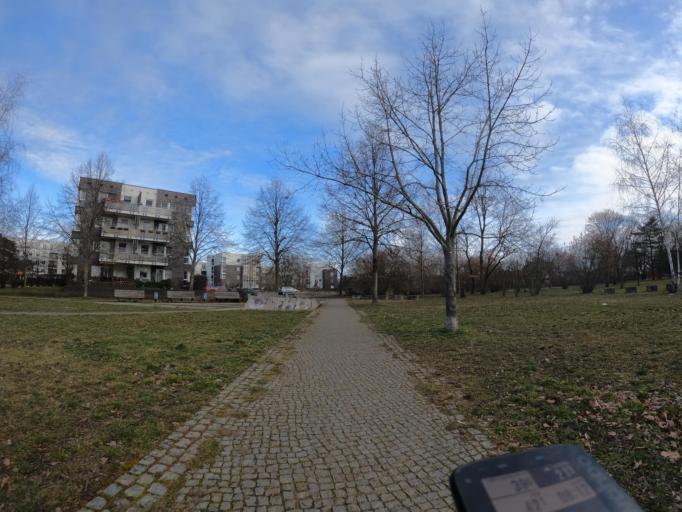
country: DE
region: Berlin
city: Altglienicke
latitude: 52.4050
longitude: 13.5461
